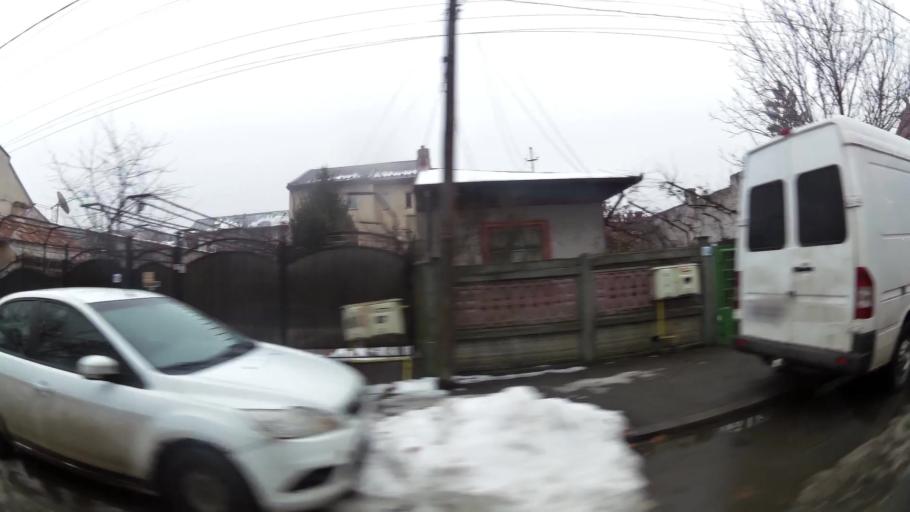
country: RO
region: Ilfov
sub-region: Comuna Chiajna
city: Rosu
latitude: 44.4738
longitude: 26.0516
